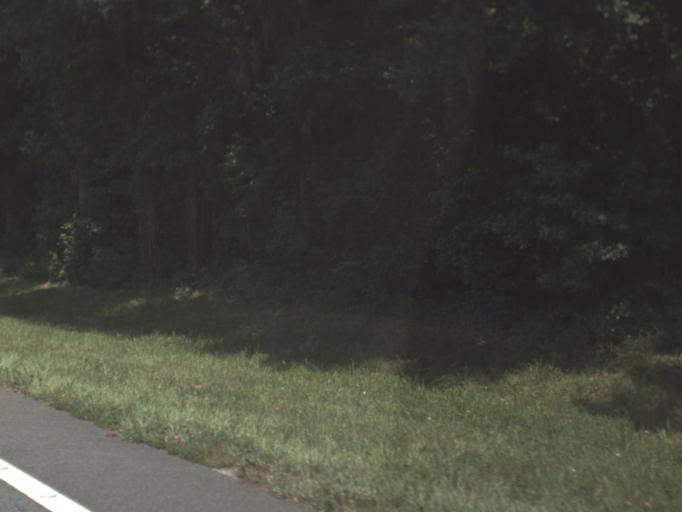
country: US
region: Florida
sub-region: Levy County
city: Williston
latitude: 29.4906
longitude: -82.4092
